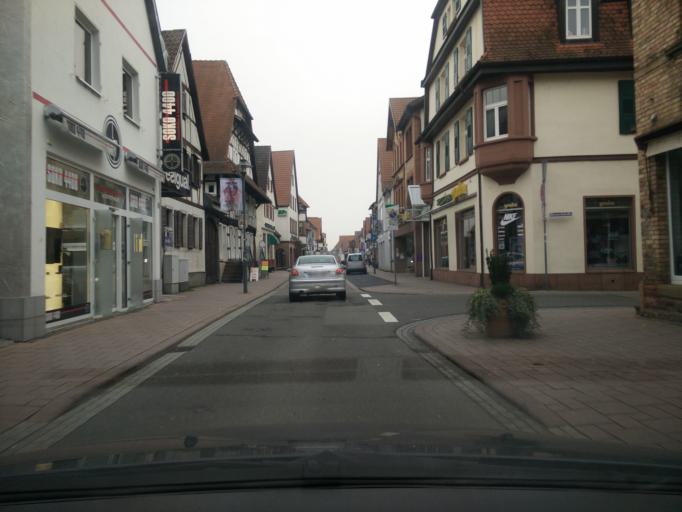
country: DE
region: Rheinland-Pfalz
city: Kandel
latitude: 49.0820
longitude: 8.1951
